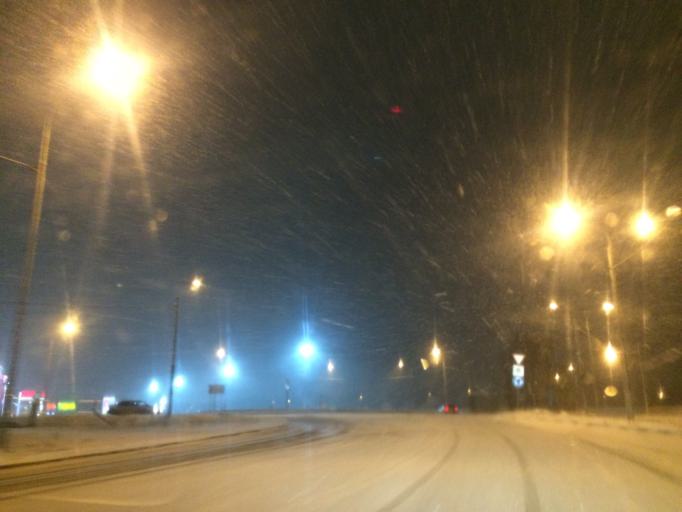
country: RU
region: Tula
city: Tula
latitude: 54.1936
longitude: 37.6315
